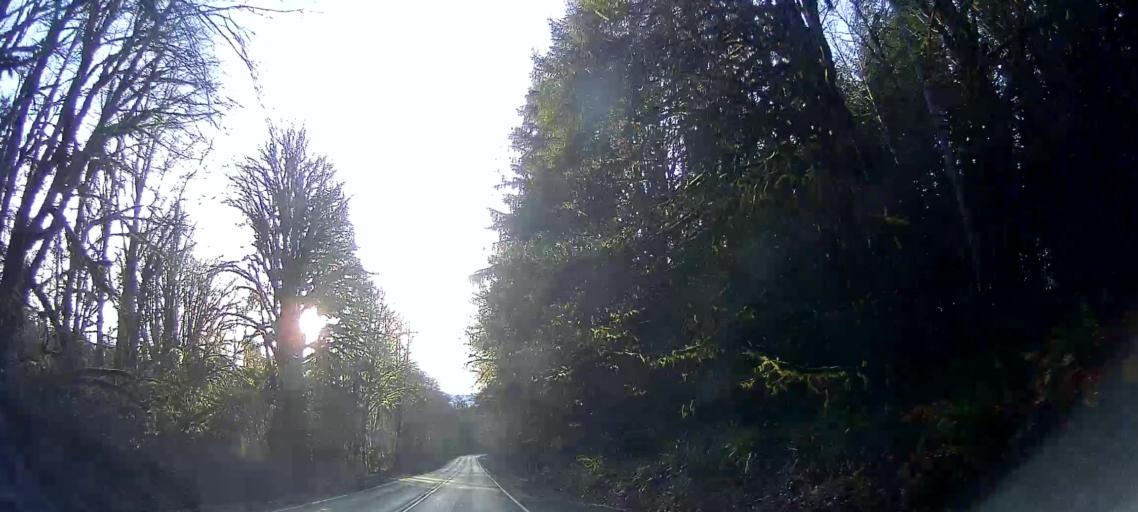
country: US
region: Washington
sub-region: Snohomish County
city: Darrington
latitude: 48.5642
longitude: -121.8119
